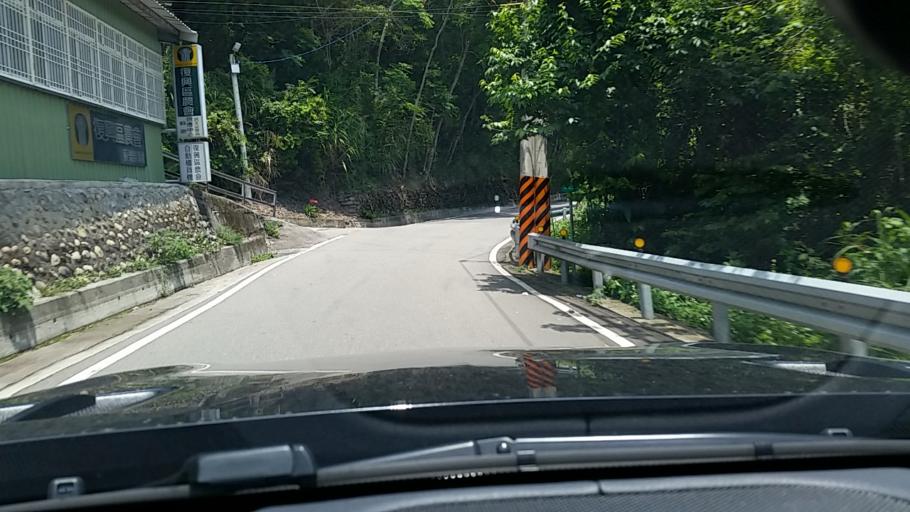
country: TW
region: Taiwan
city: Daxi
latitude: 24.6950
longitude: 121.3744
